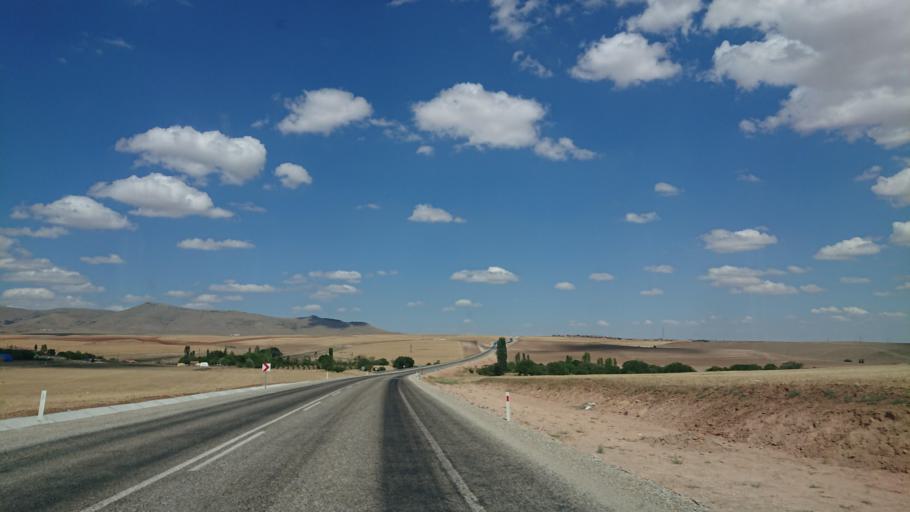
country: TR
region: Ankara
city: Evren
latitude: 39.1221
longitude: 33.9558
